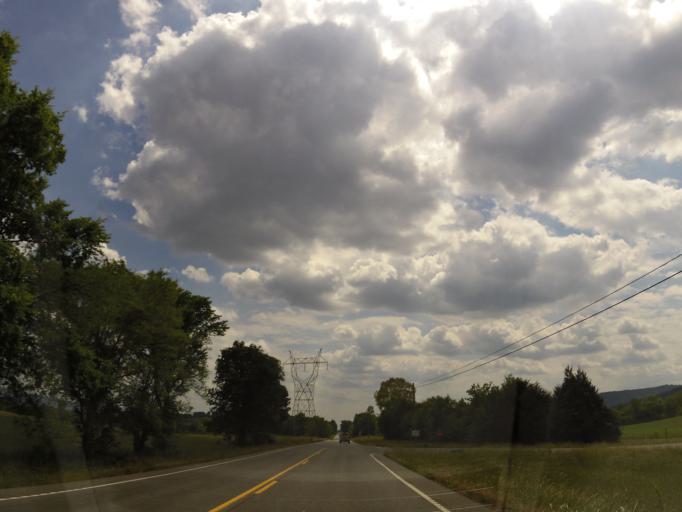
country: US
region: Tennessee
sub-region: Sequatchie County
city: Dunlap
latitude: 35.4348
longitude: -85.3504
